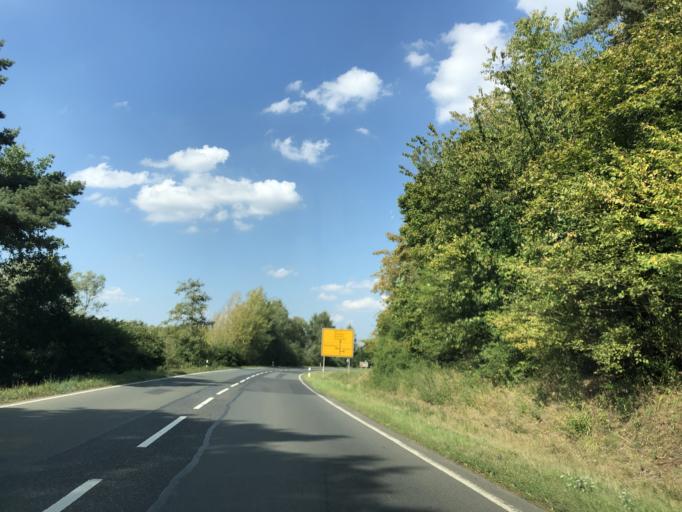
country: DE
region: Hesse
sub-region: Regierungsbezirk Giessen
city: Rauschenberg
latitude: 50.8734
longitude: 8.9368
